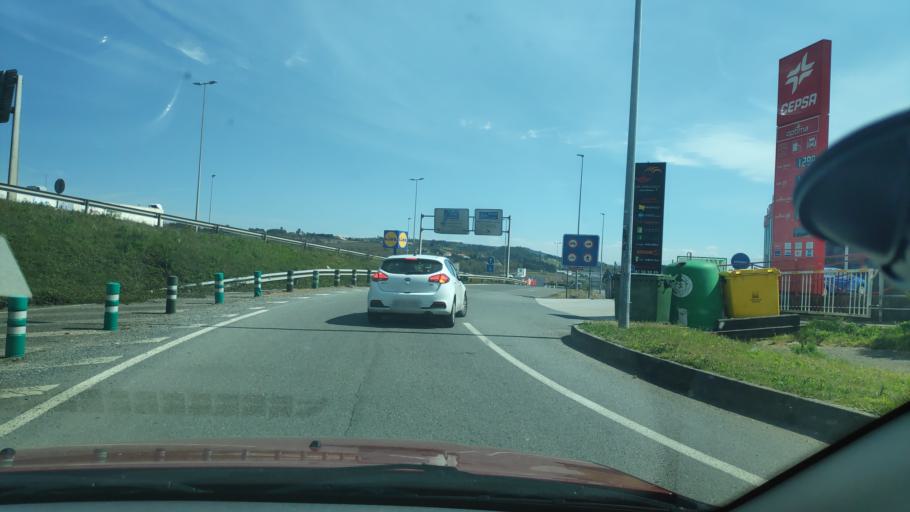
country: ES
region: Galicia
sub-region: Provincia da Coruna
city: Santiago de Compostela
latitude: 42.9021
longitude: -8.5119
